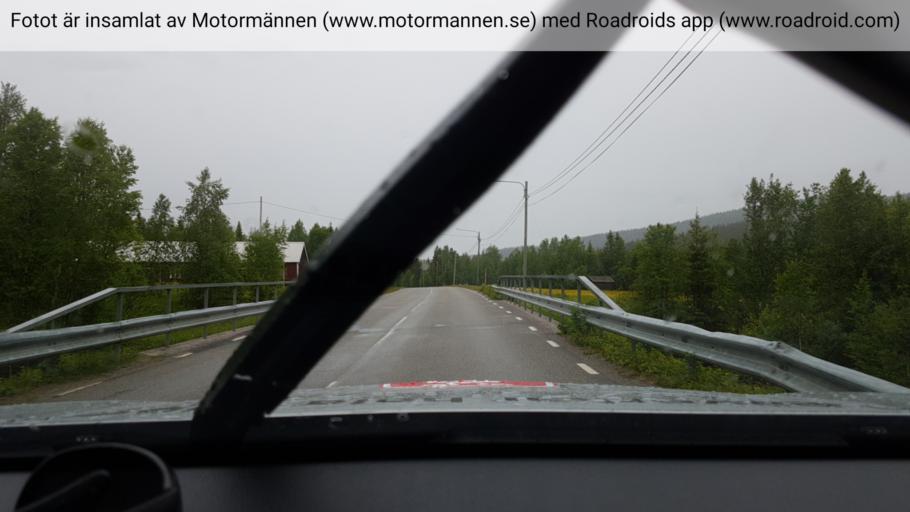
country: SE
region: Vaesterbotten
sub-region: Storumans Kommun
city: Fristad
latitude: 65.8871
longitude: 16.3676
